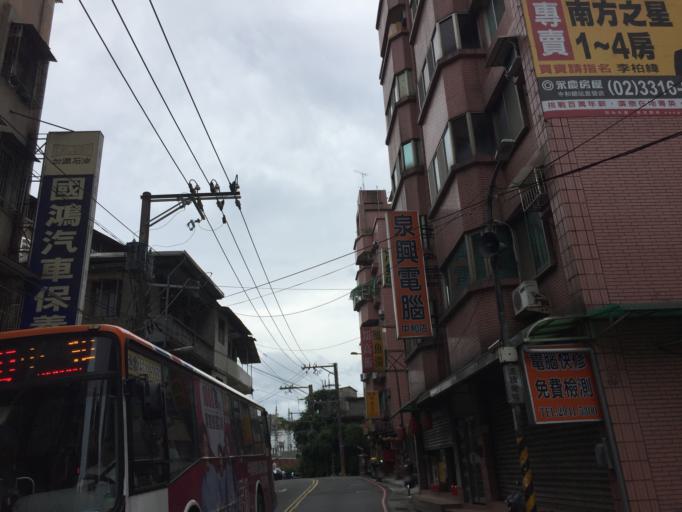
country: TW
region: Taipei
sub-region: Taipei
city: Banqiao
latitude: 24.9899
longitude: 121.5068
